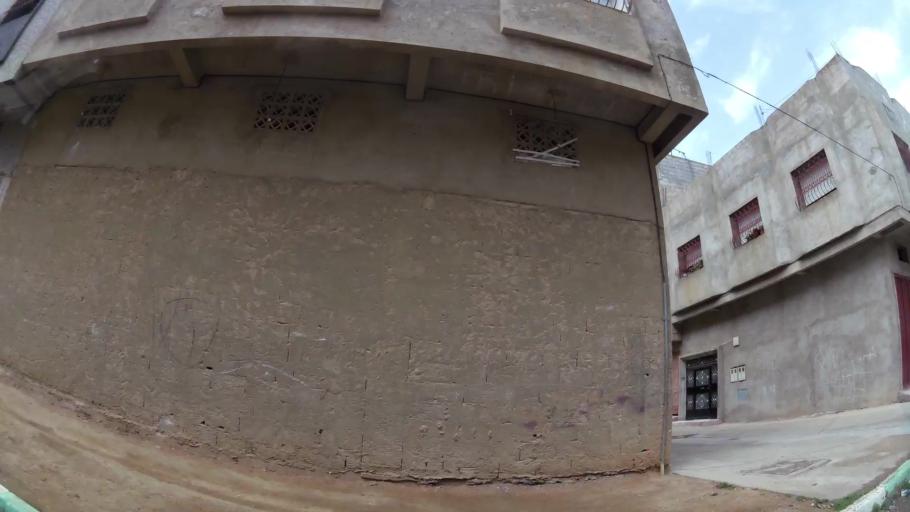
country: MA
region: Rabat-Sale-Zemmour-Zaer
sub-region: Khemisset
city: Tiflet
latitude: 33.8902
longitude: -6.3282
